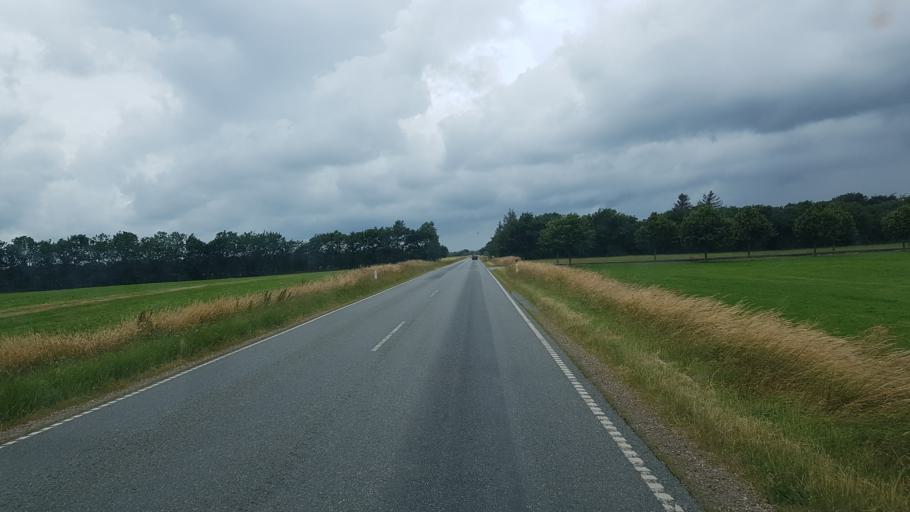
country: DK
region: South Denmark
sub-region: Kolding Kommune
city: Vamdrup
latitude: 55.4346
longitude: 9.2112
